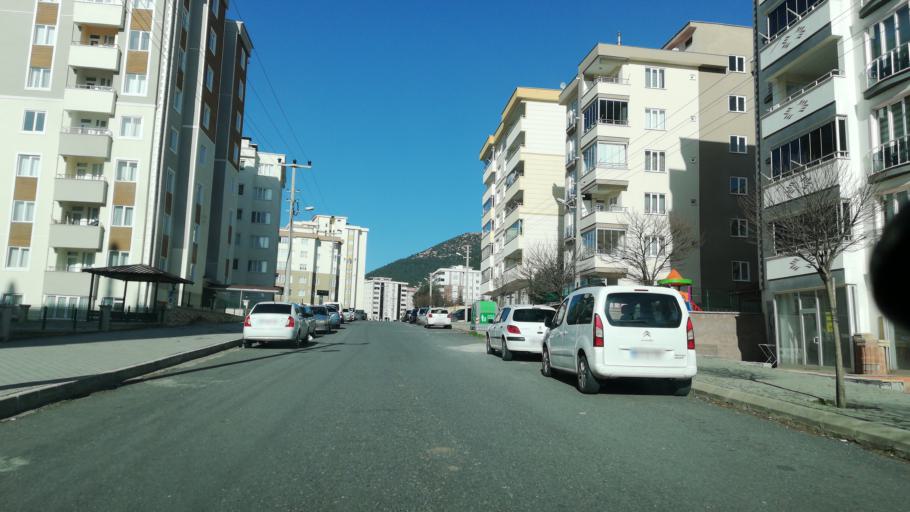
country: TR
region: Kahramanmaras
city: Kahramanmaras
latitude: 37.5982
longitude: 36.8875
